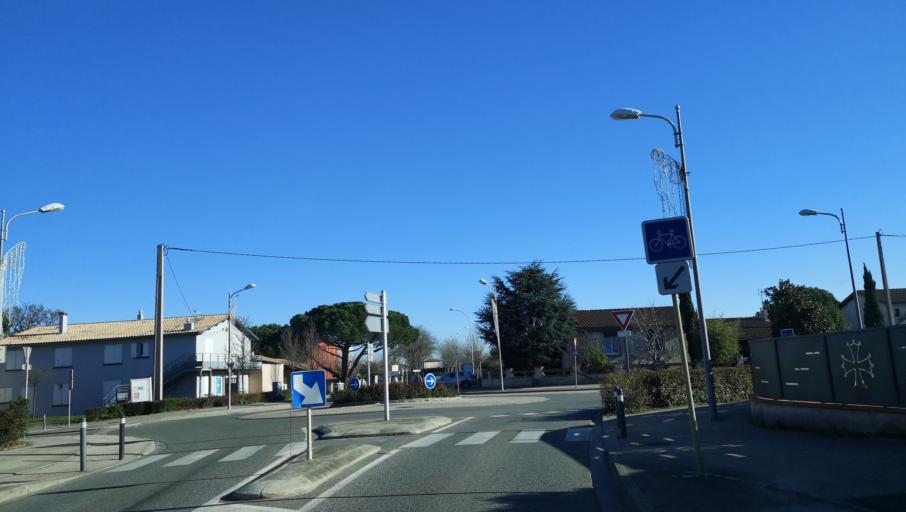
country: FR
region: Midi-Pyrenees
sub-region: Departement de la Haute-Garonne
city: Beauzelle
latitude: 43.6510
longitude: 1.3849
